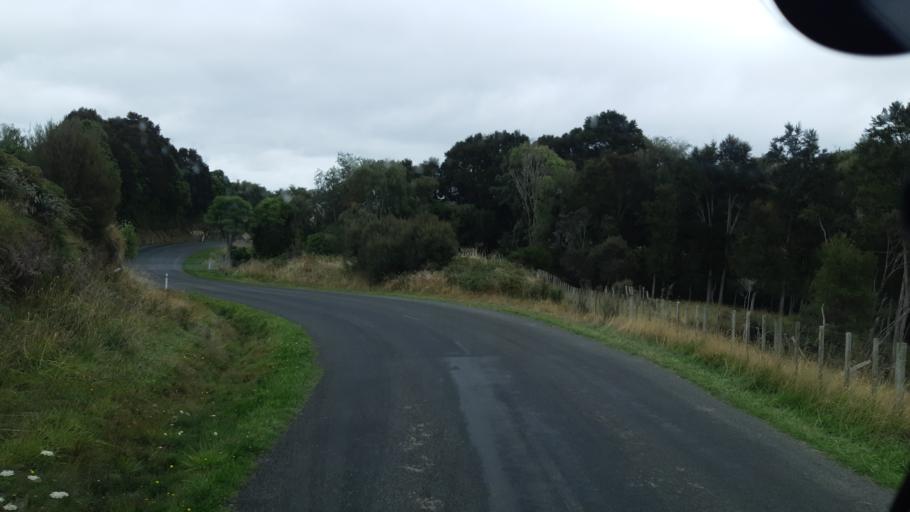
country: NZ
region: Manawatu-Wanganui
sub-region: Ruapehu District
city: Waiouru
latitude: -39.5527
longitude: 175.6414
